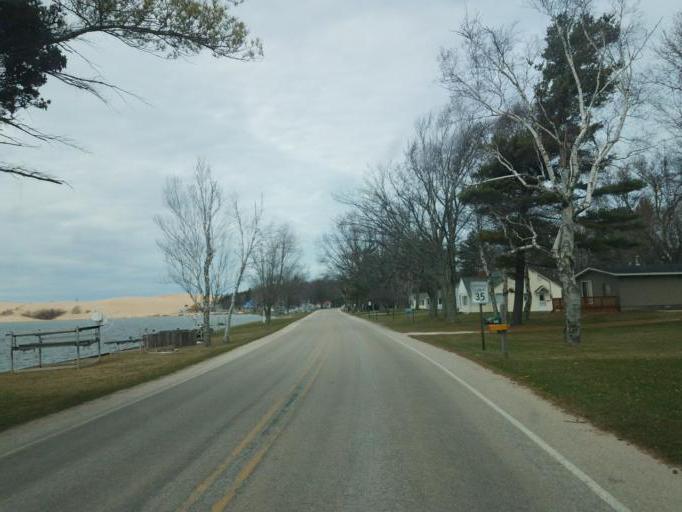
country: US
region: Michigan
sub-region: Oceana County
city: Hart
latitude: 43.6763
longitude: -86.4950
